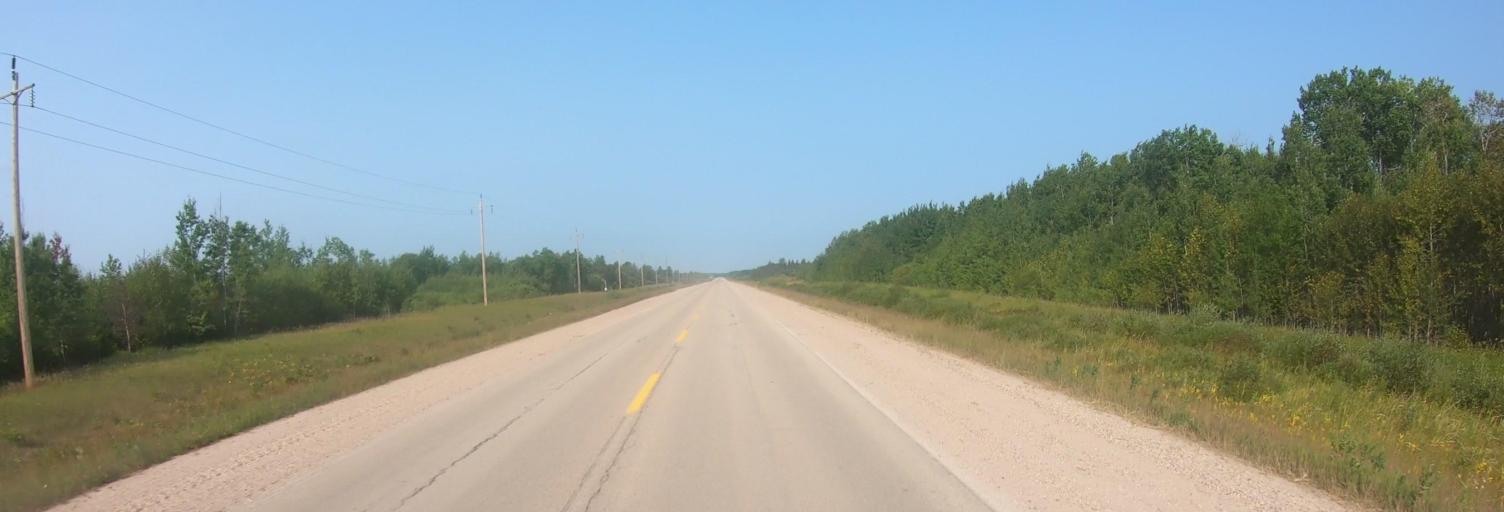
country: US
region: Minnesota
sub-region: Roseau County
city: Roseau
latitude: 49.0234
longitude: -95.6820
